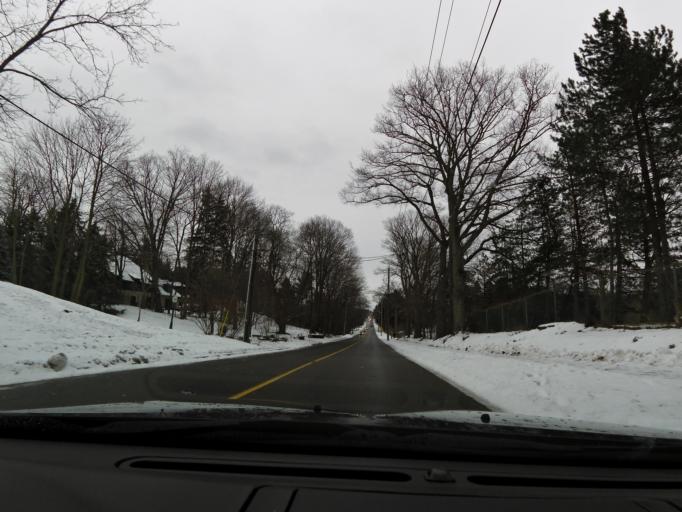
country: CA
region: Ontario
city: Ancaster
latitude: 43.2217
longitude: -79.9757
